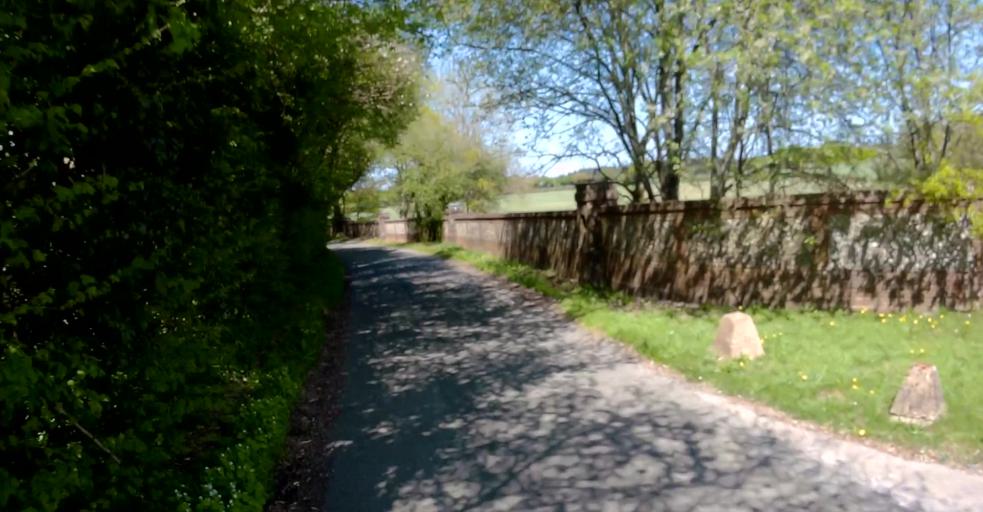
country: GB
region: England
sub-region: Hampshire
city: Overton
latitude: 51.2001
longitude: -1.2834
